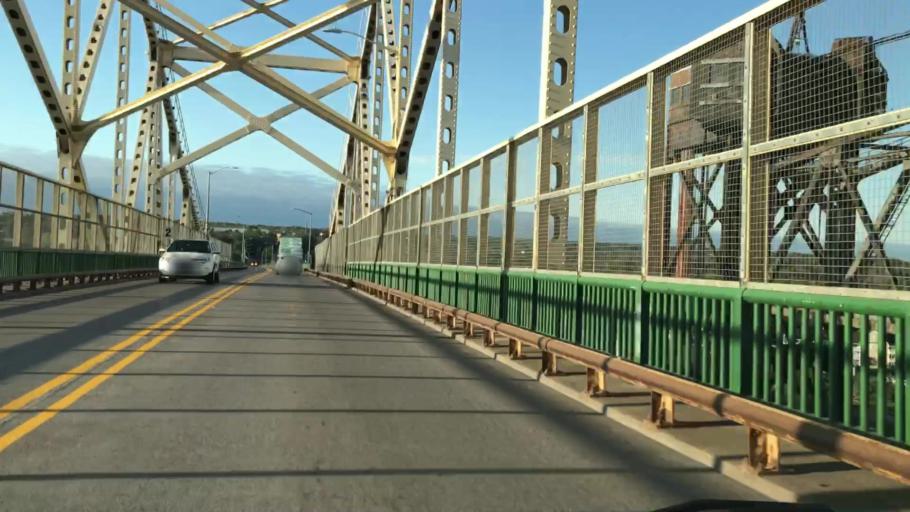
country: US
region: Michigan
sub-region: Chippewa County
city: Sault Ste. Marie
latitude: 46.5022
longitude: -84.3634
